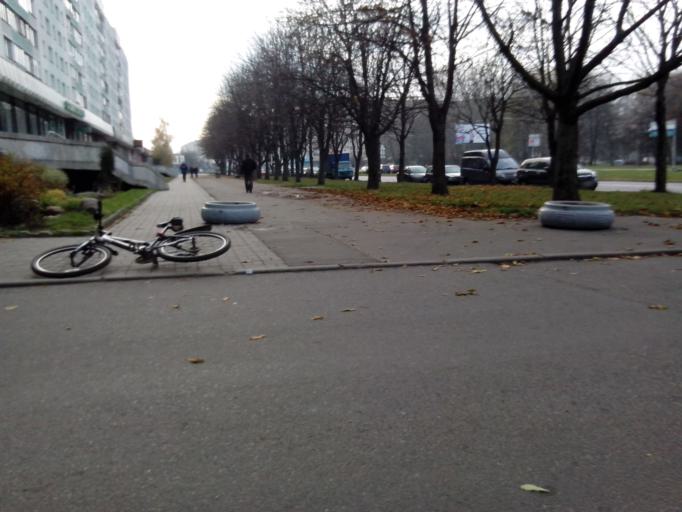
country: BY
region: Minsk
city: Minsk
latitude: 53.9281
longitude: 27.5738
